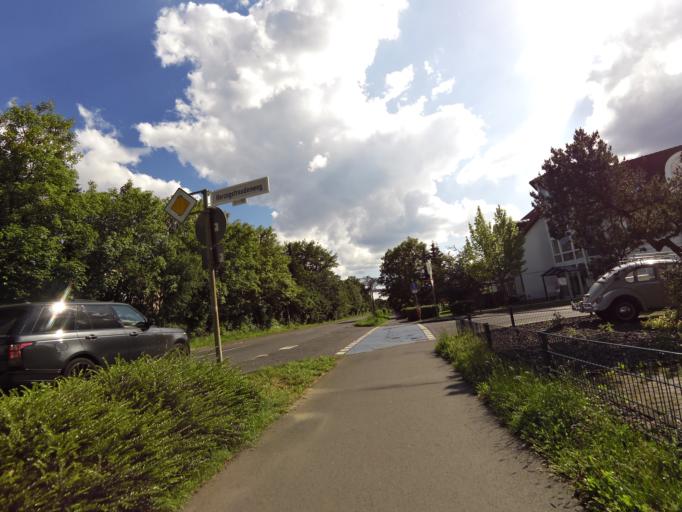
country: DE
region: North Rhine-Westphalia
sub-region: Regierungsbezirk Koln
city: Wachtberg
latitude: 50.6767
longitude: 7.0695
